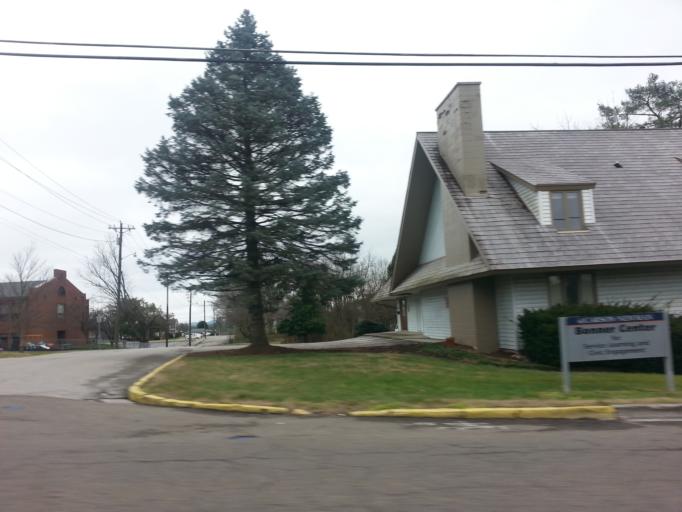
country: US
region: Tennessee
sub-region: Jefferson County
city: Jefferson City
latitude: 36.1199
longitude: -83.4923
